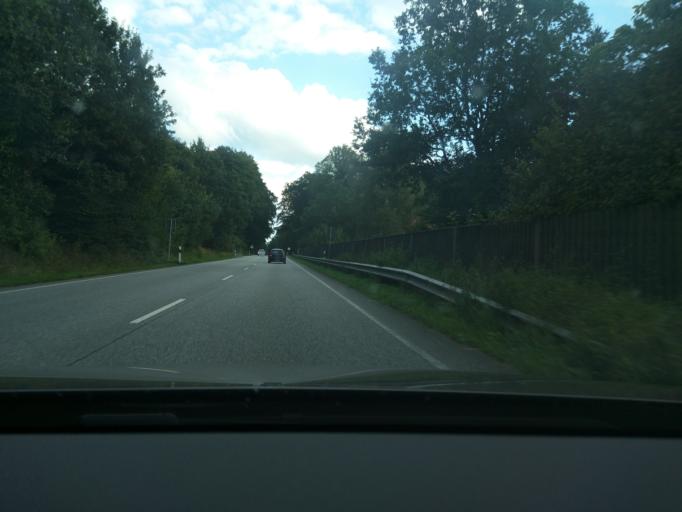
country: DE
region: Schleswig-Holstein
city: Kasseburg
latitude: 53.5500
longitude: 10.4166
